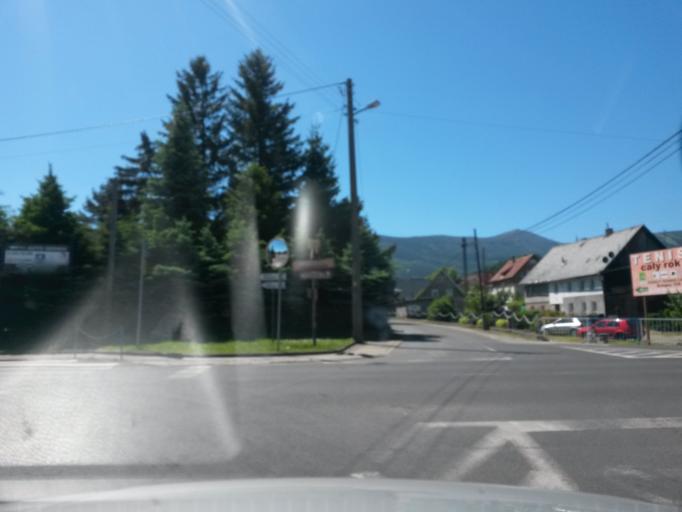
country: PL
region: Lower Silesian Voivodeship
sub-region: Powiat jeleniogorski
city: Karpacz
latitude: 50.7929
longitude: 15.7778
